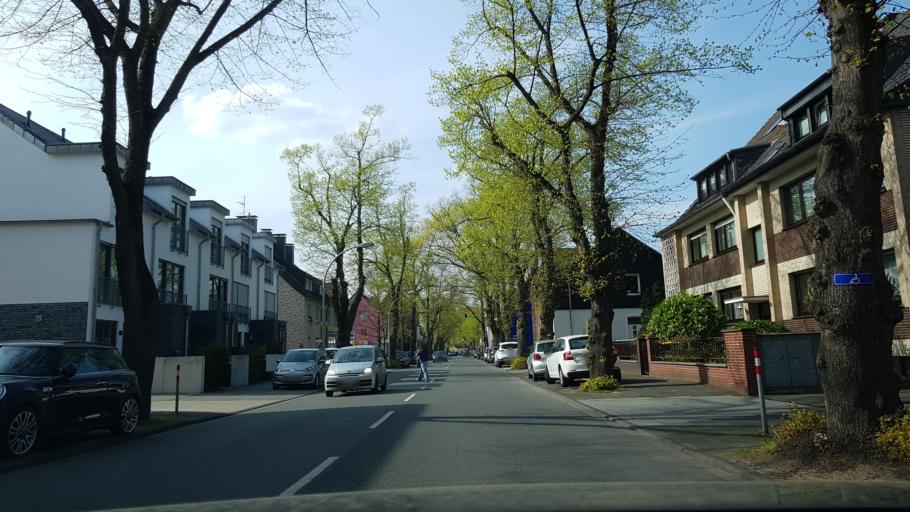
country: DE
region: North Rhine-Westphalia
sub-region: Regierungsbezirk Dusseldorf
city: Hochfeld
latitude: 51.3816
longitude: 6.7806
